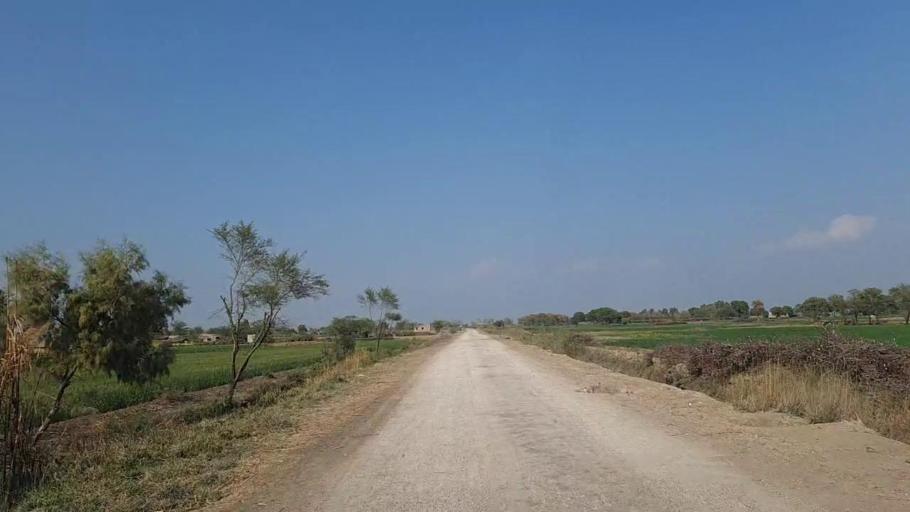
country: PK
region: Sindh
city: Jam Sahib
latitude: 26.2941
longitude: 68.5832
